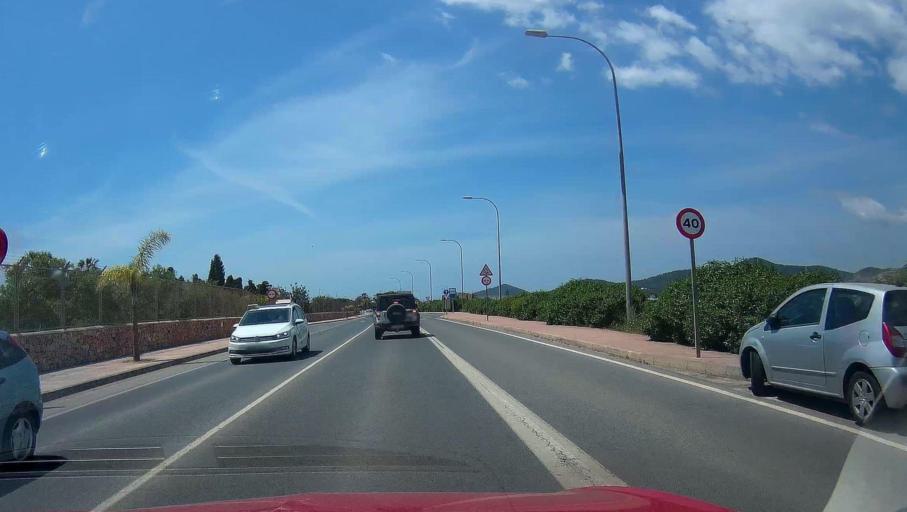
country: ES
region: Balearic Islands
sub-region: Illes Balears
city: Ibiza
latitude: 38.8803
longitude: 1.3726
